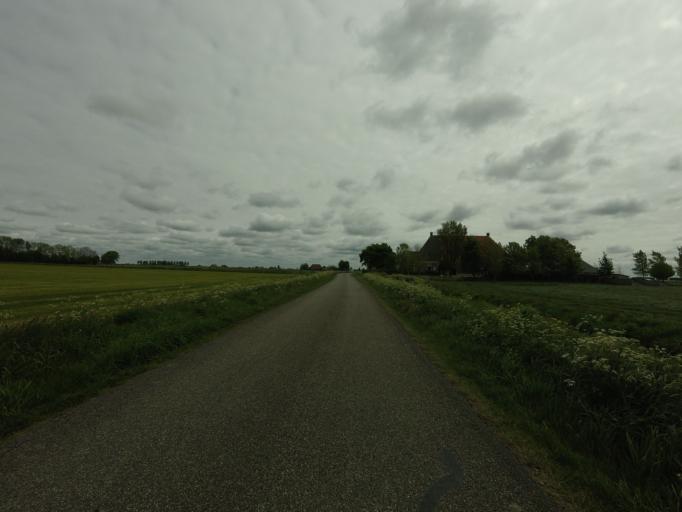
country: NL
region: Friesland
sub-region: Sudwest Fryslan
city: Workum
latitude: 52.9585
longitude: 5.4719
